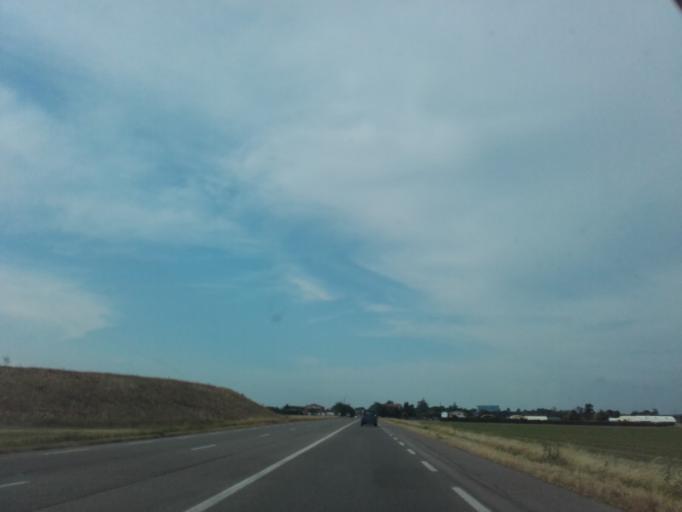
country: FR
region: Rhone-Alpes
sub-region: Departement de la Drome
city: Etoile-sur-Rhone
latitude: 44.8272
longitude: 4.8622
